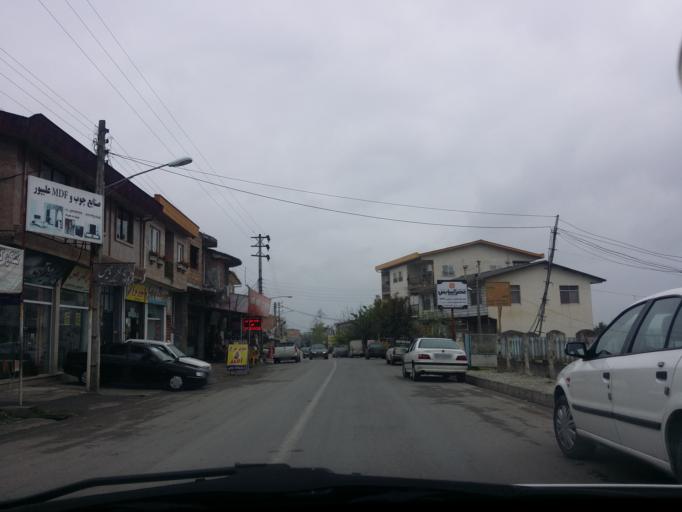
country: IR
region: Mazandaran
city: Chalus
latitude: 36.6639
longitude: 51.3927
